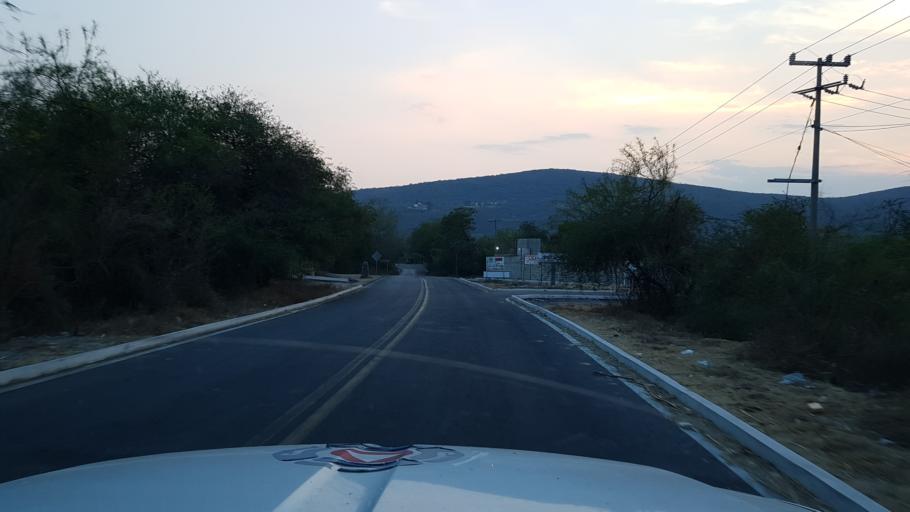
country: MX
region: Morelos
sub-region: Tlaltizapan de Zapata
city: Colonia Palo Prieto (Chipitongo)
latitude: 18.7156
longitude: -99.1070
